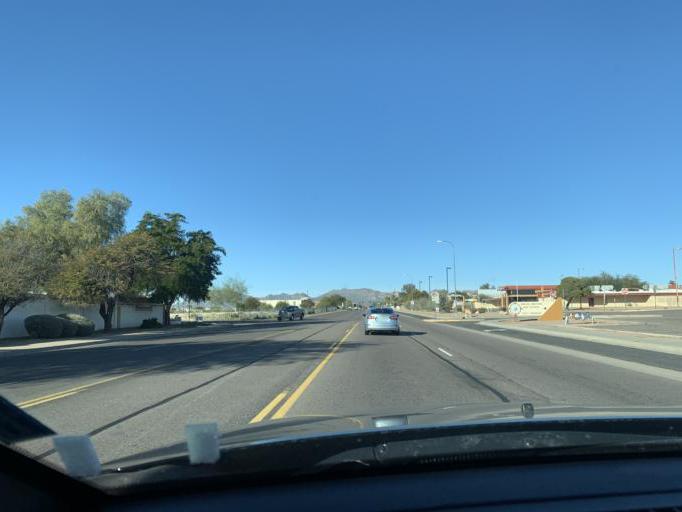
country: US
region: Arizona
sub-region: Pinal County
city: Apache Junction
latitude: 33.3891
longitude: -111.5633
